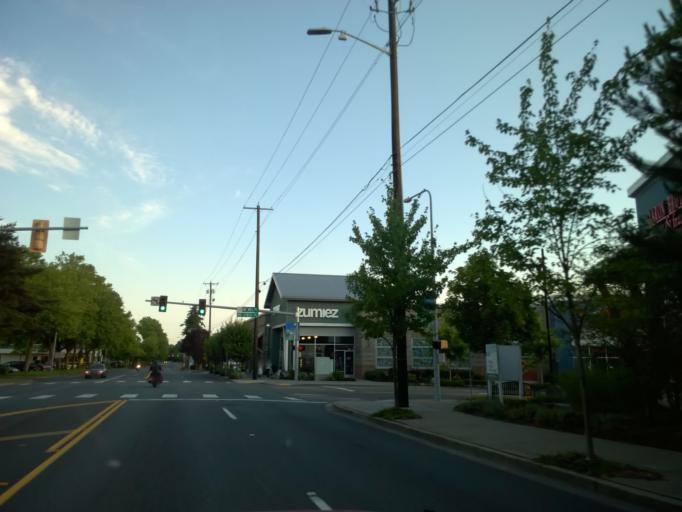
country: US
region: Washington
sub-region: King County
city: Woodinville
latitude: 47.7562
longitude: -122.1529
